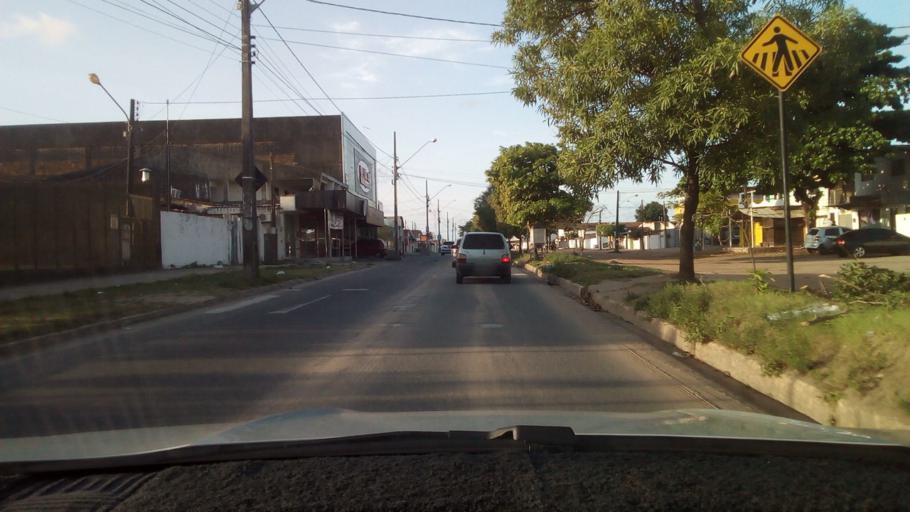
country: BR
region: Paraiba
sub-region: Conde
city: Conde
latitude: -7.2017
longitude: -34.8537
